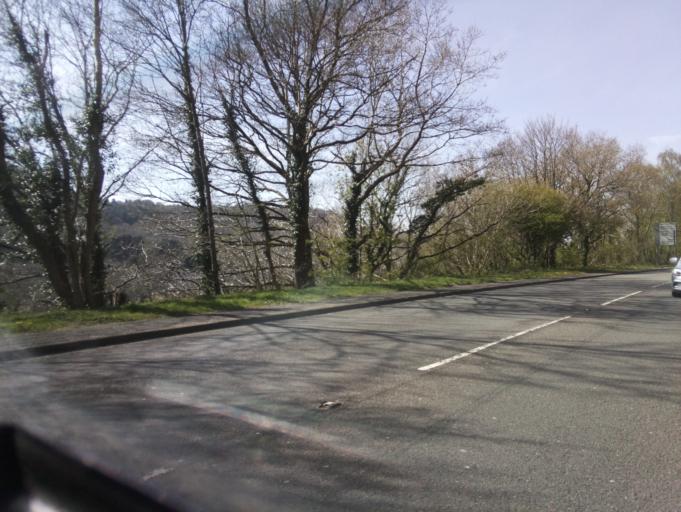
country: GB
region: Wales
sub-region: Merthyr Tydfil County Borough
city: Treharris
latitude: 51.6547
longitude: -3.3328
